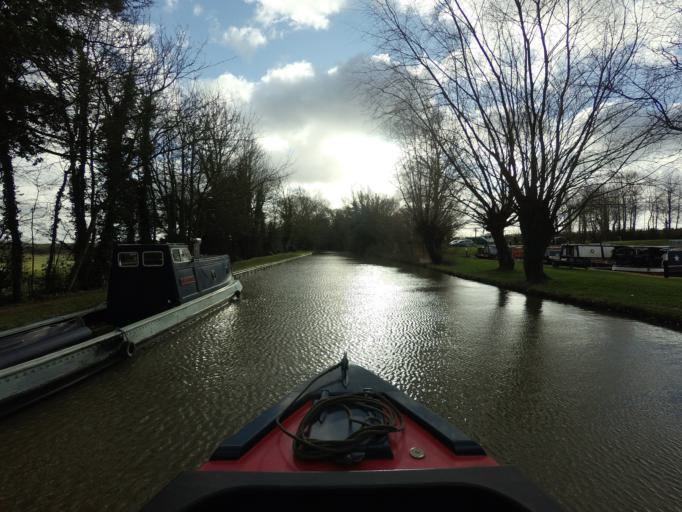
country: GB
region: England
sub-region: Northamptonshire
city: Long Buckby
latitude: 52.2901
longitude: -1.1219
